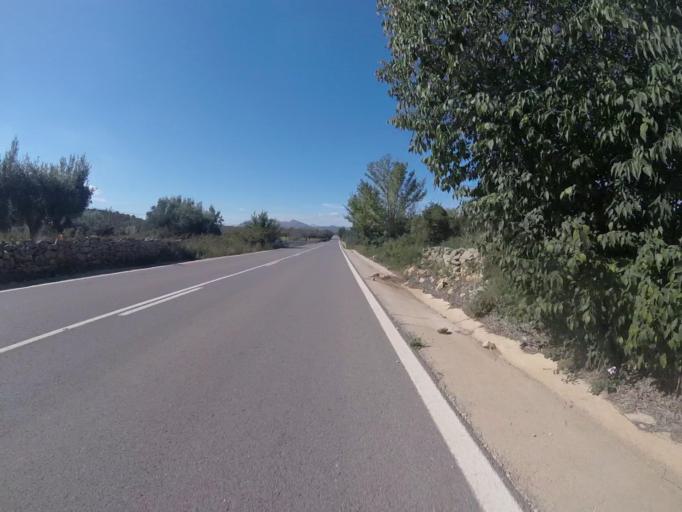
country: ES
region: Valencia
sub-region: Provincia de Castello
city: Albocasser
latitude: 40.3526
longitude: 0.0154
